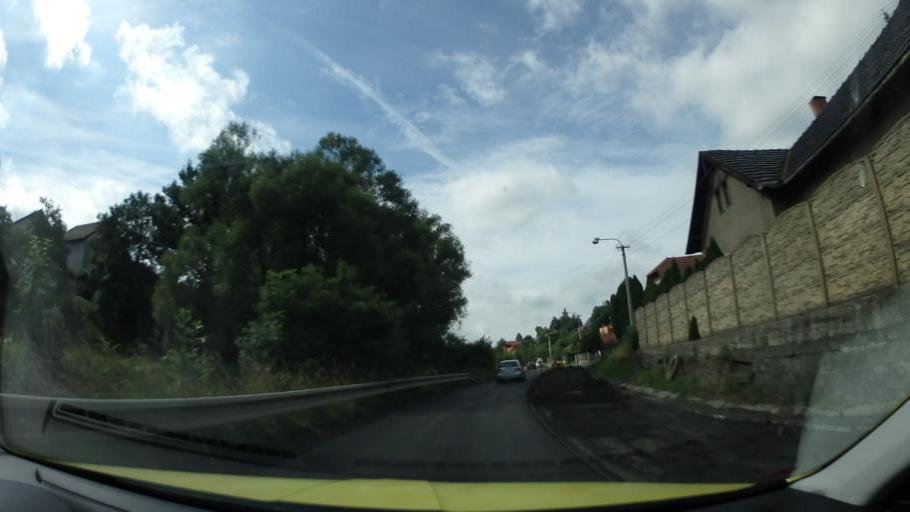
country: CZ
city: Hodslavice
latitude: 49.5519
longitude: 18.0261
